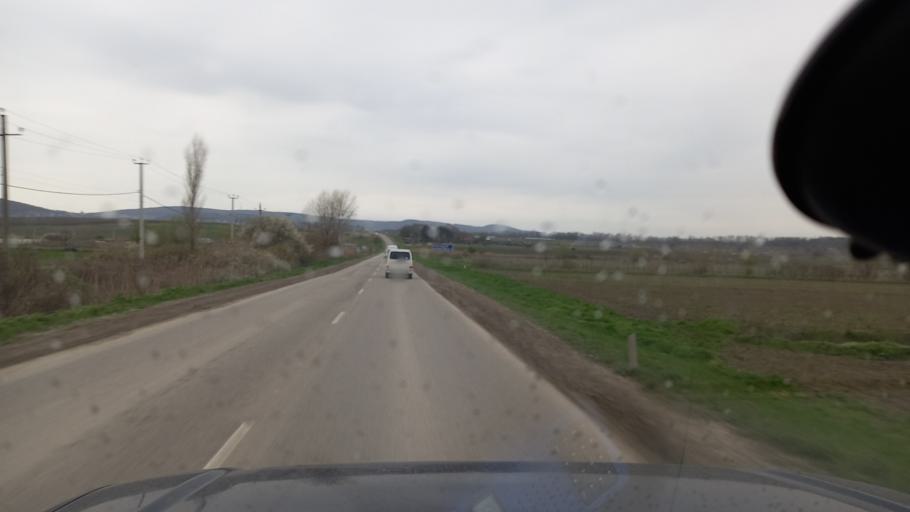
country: RU
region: Krasnodarskiy
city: Anapskaya
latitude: 44.8889
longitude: 37.4586
